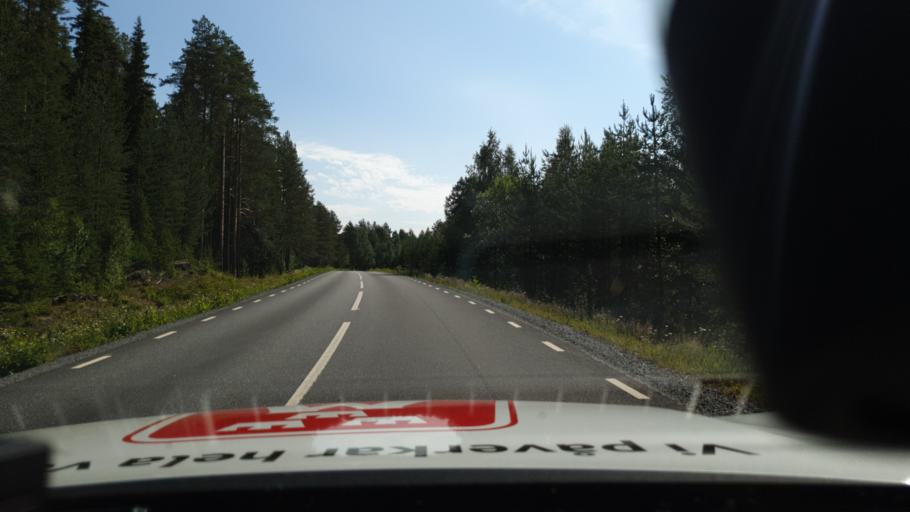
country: SE
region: Norrbotten
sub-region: Bodens Kommun
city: Saevast
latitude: 65.8382
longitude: 21.8325
